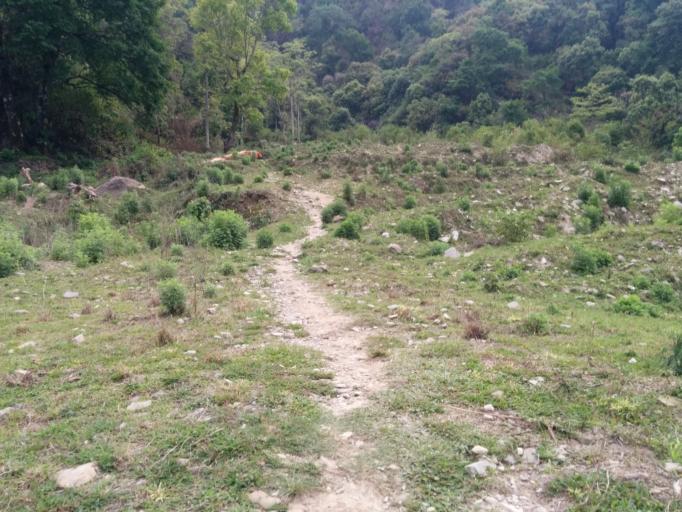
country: NP
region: Western Region
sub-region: Gandaki Zone
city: Pokhara
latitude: 28.2316
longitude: 83.9498
